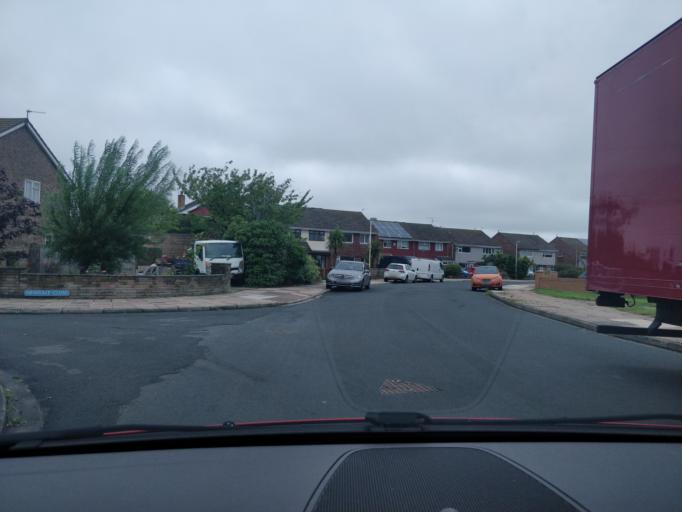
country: GB
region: England
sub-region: Lancashire
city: Banks
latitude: 53.6769
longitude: -2.9611
